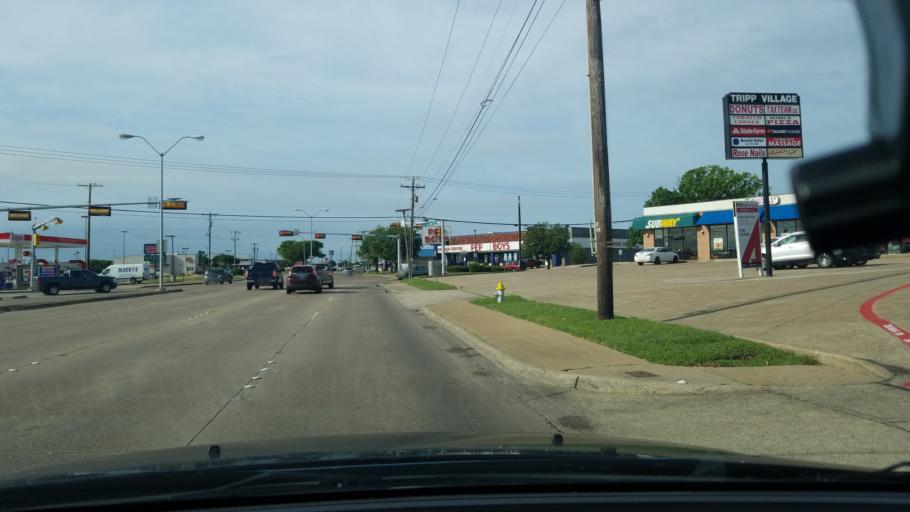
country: US
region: Texas
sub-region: Dallas County
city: Mesquite
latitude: 32.7980
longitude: -96.6118
